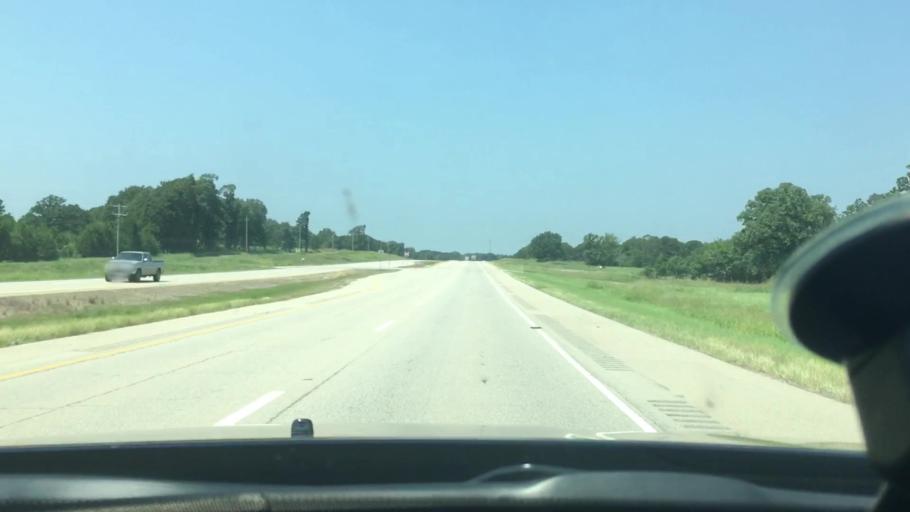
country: US
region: Oklahoma
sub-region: Atoka County
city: Atoka
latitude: 34.3127
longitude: -96.0216
